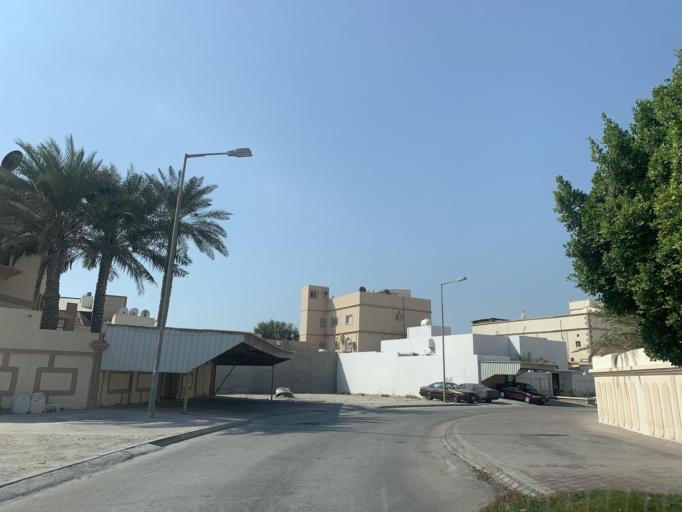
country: BH
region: Central Governorate
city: Madinat Hamad
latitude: 26.1105
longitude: 50.4965
